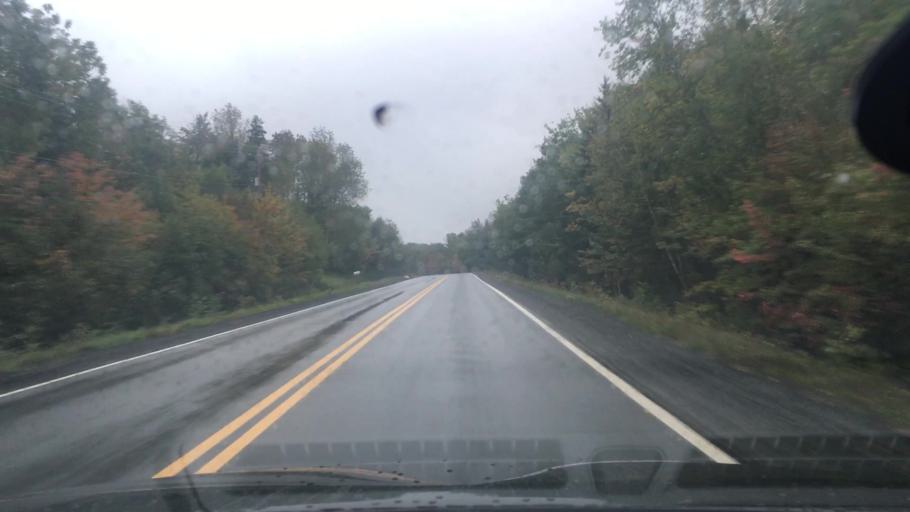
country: CA
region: Nova Scotia
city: Windsor
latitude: 44.8445
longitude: -64.2267
